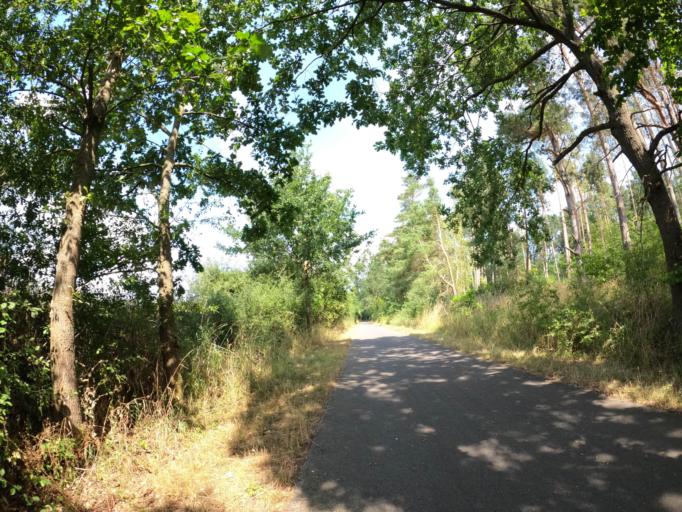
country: DE
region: Mecklenburg-Vorpommern
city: Woldegk
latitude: 53.3113
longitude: 13.5759
